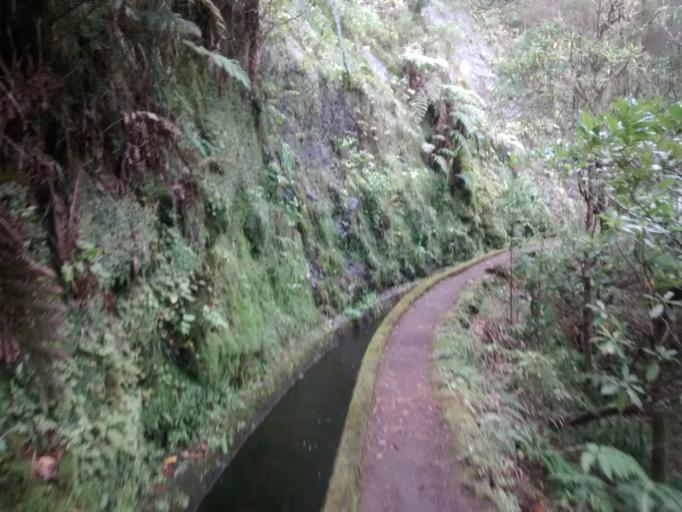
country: PT
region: Madeira
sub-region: Sao Vicente
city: Sao Vicente
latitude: 32.7523
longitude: -17.0390
